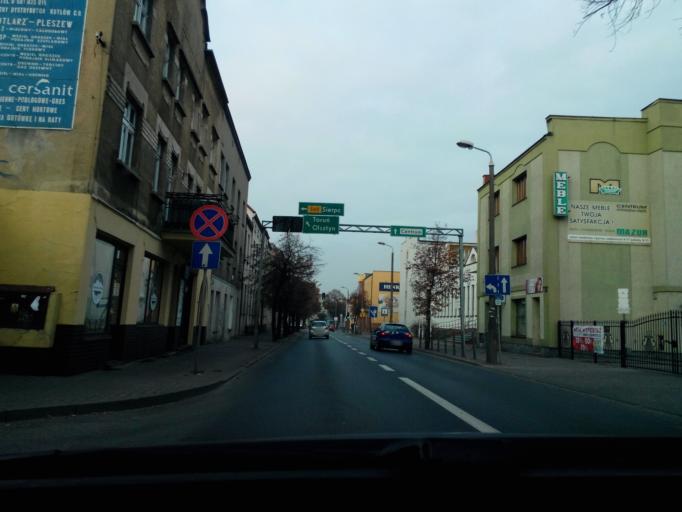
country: PL
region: Kujawsko-Pomorskie
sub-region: Powiat brodnicki
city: Brodnica
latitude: 53.2515
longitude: 19.4003
